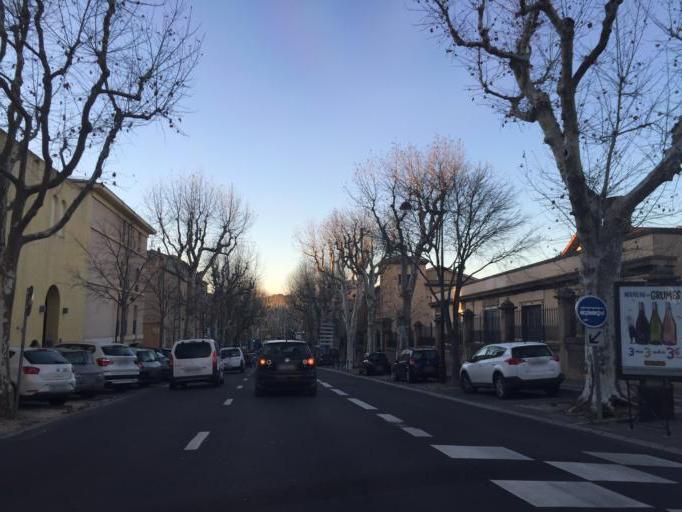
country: FR
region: Provence-Alpes-Cote d'Azur
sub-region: Departement des Bouches-du-Rhone
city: Aix-en-Provence
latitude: 43.5286
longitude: 5.4546
